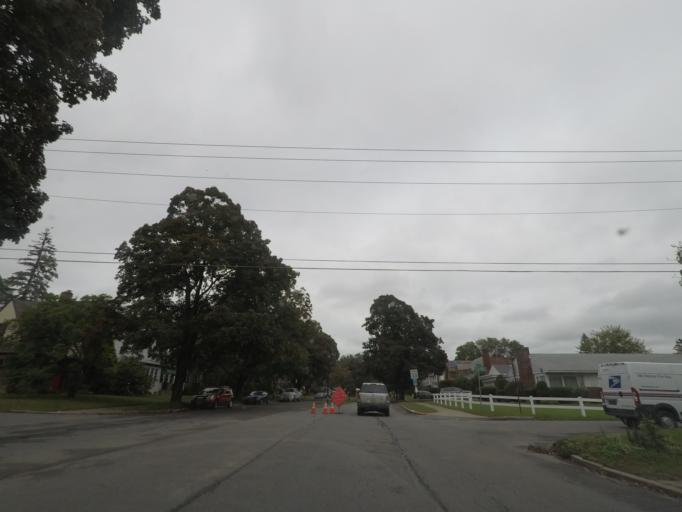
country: US
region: New York
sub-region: Albany County
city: West Albany
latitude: 42.6537
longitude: -73.8007
